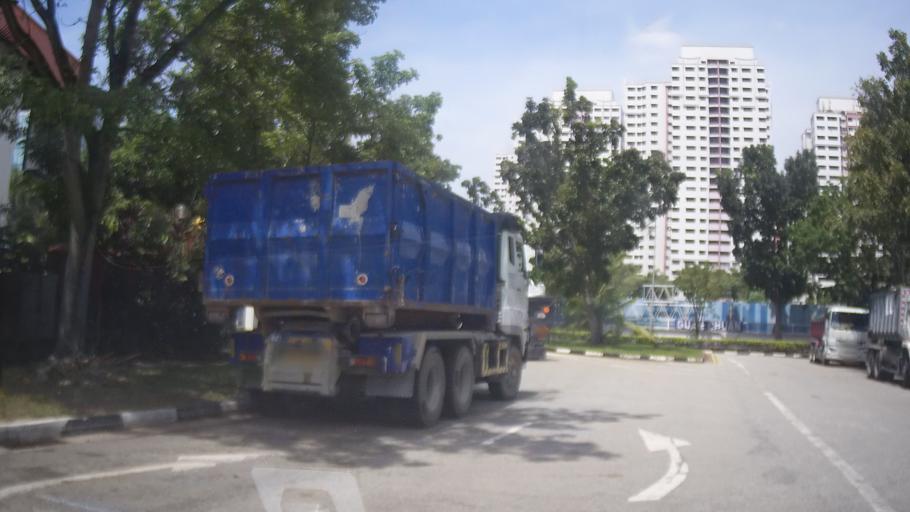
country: MY
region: Johor
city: Johor Bahru
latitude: 1.4058
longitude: 103.7523
